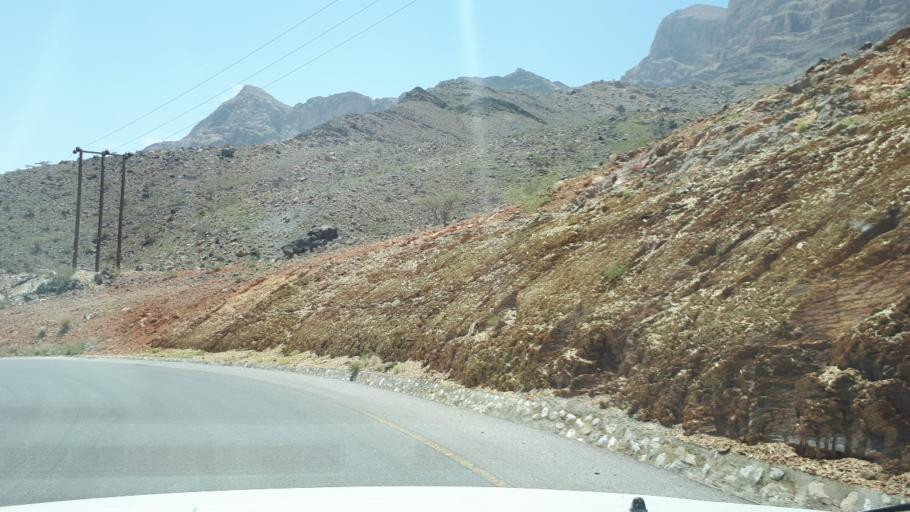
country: OM
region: Muhafazat ad Dakhiliyah
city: Bahla'
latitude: 23.1947
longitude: 57.1372
